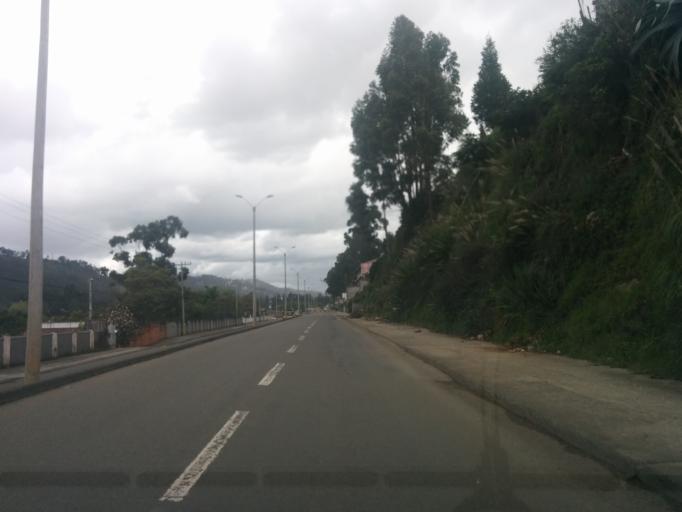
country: EC
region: Azuay
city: Cuenca
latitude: -2.8867
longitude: -78.9589
